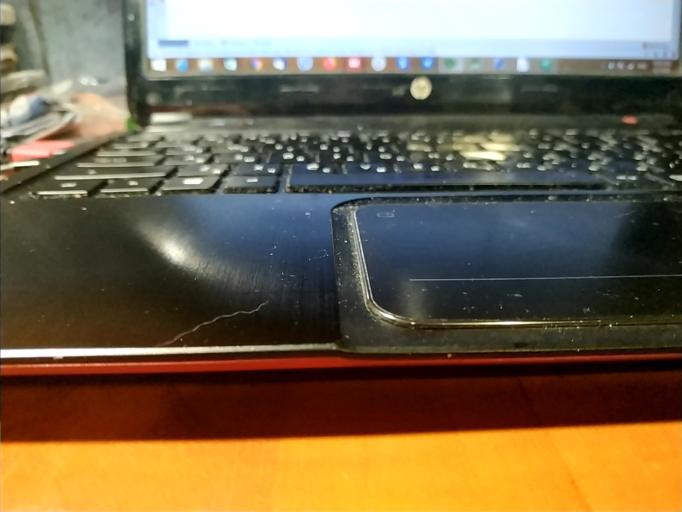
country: RU
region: Vologda
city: Suda
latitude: 58.9143
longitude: 37.5432
